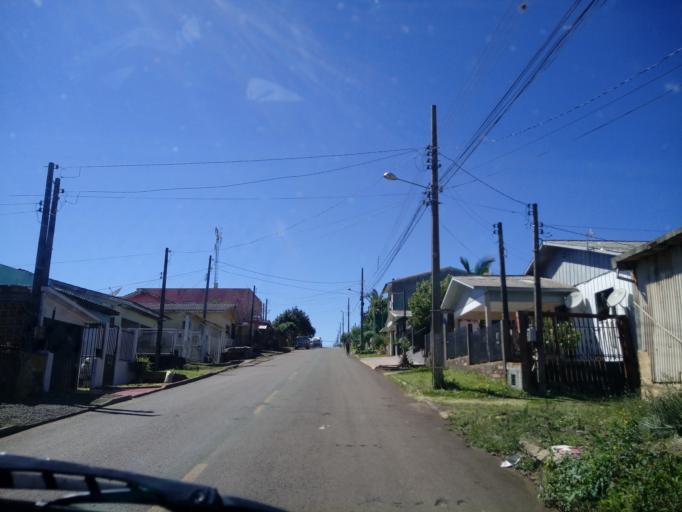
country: BR
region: Santa Catarina
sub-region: Chapeco
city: Chapeco
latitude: -27.0890
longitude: -52.6808
